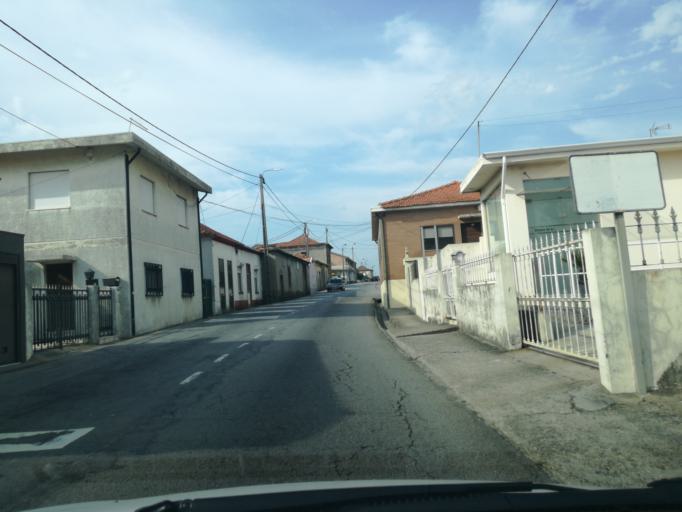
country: PT
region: Aveiro
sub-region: Espinho
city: Espinho
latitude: 41.0177
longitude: -8.6320
